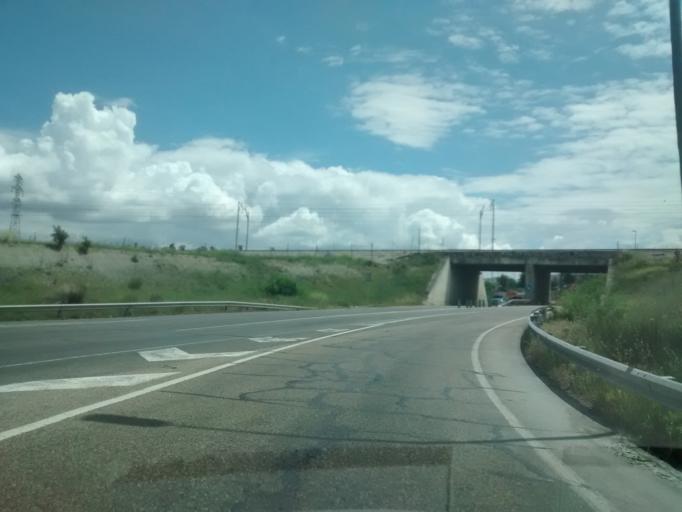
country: ES
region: Madrid
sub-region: Provincia de Madrid
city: Coslada
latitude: 40.4390
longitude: -3.5602
